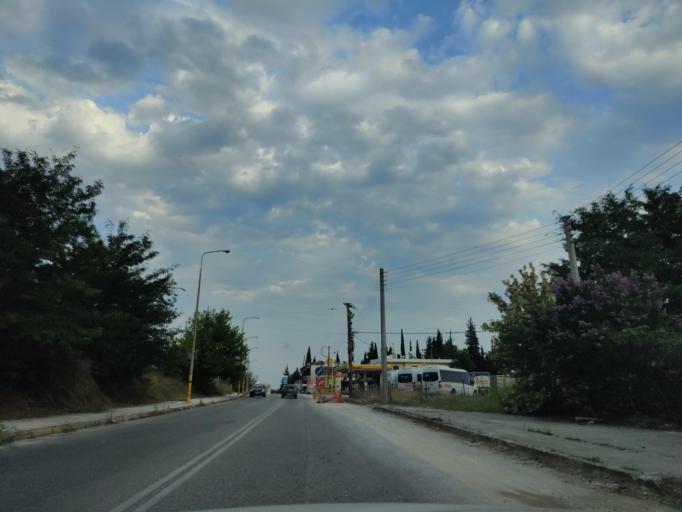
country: GR
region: East Macedonia and Thrace
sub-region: Nomos Dramas
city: Drama
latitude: 41.1517
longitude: 24.1333
